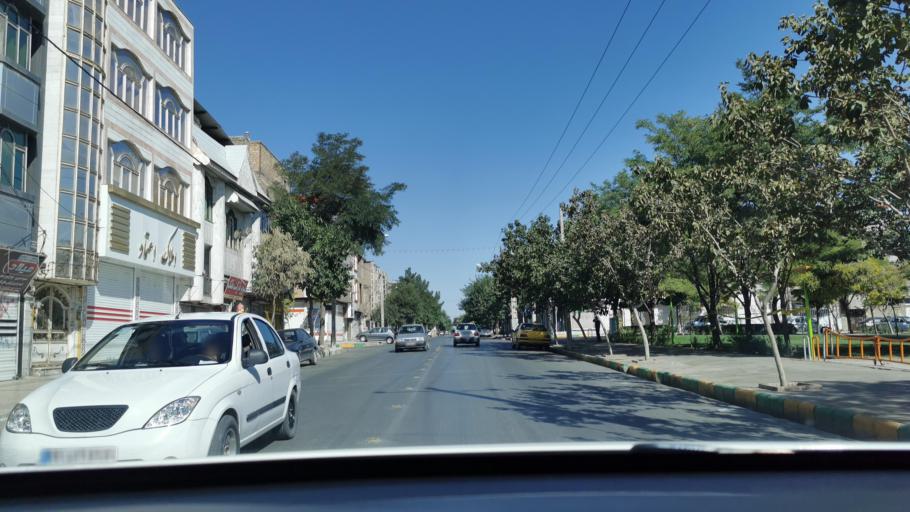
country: IR
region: Razavi Khorasan
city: Mashhad
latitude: 36.3334
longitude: 59.6405
